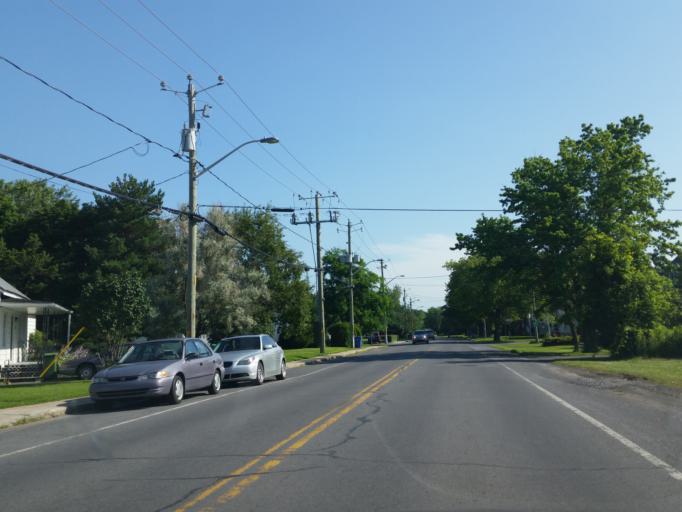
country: CA
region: Quebec
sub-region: Monteregie
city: Napierville
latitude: 45.1921
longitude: -73.4016
